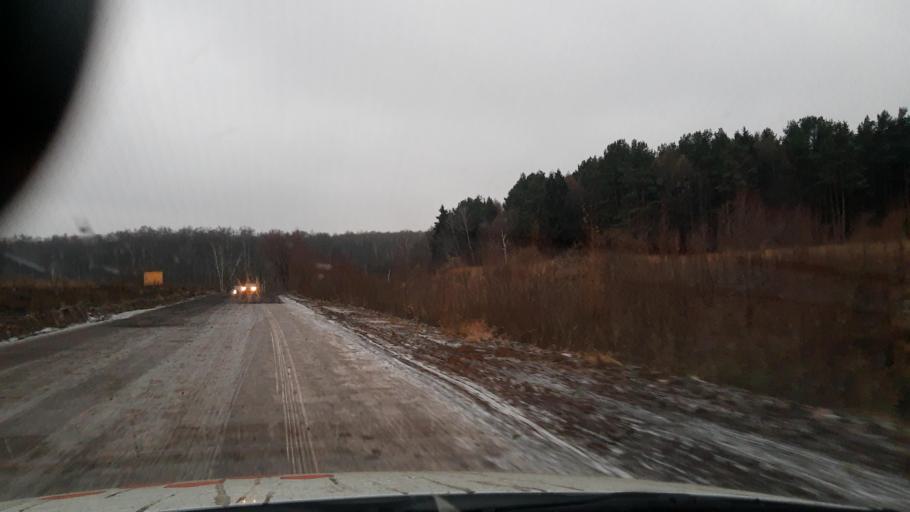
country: RU
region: Moscow
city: Solntsevo
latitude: 55.6263
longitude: 37.3838
